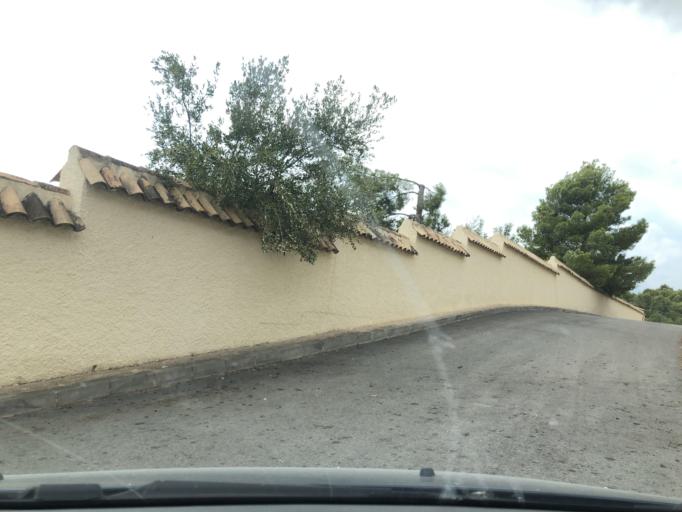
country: ES
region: Valencia
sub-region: Provincia de Alicante
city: Altea
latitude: 38.6411
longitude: -0.0684
